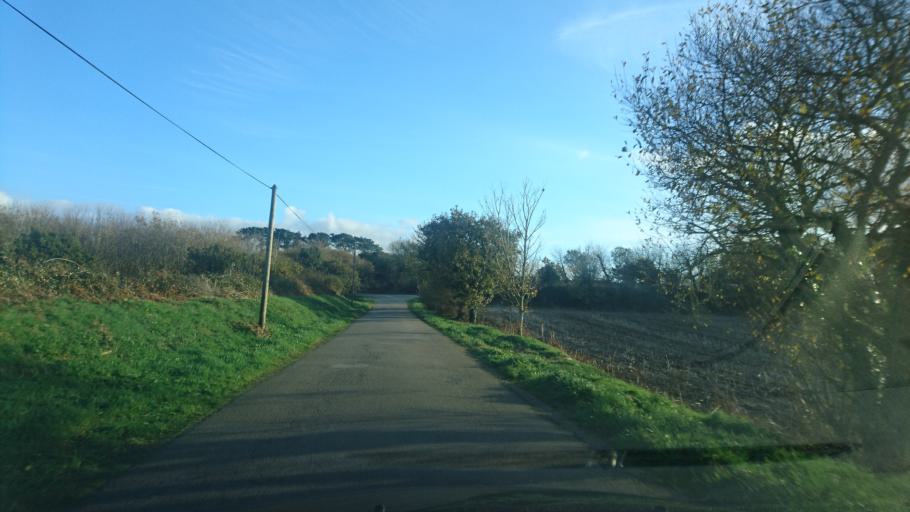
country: FR
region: Brittany
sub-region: Departement du Finistere
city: Lampaul-Plouarzel
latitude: 48.4372
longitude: -4.7595
